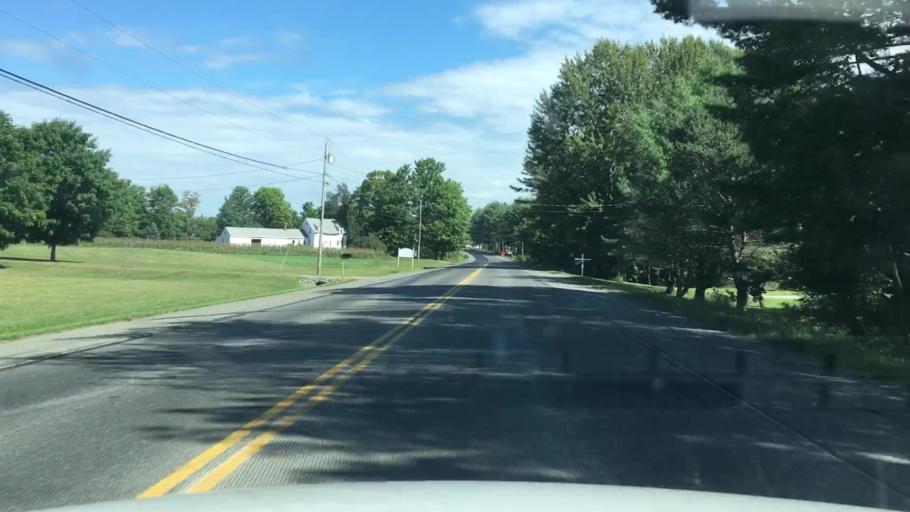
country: US
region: Maine
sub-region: Penobscot County
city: Corinna
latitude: 44.8987
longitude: -69.2678
